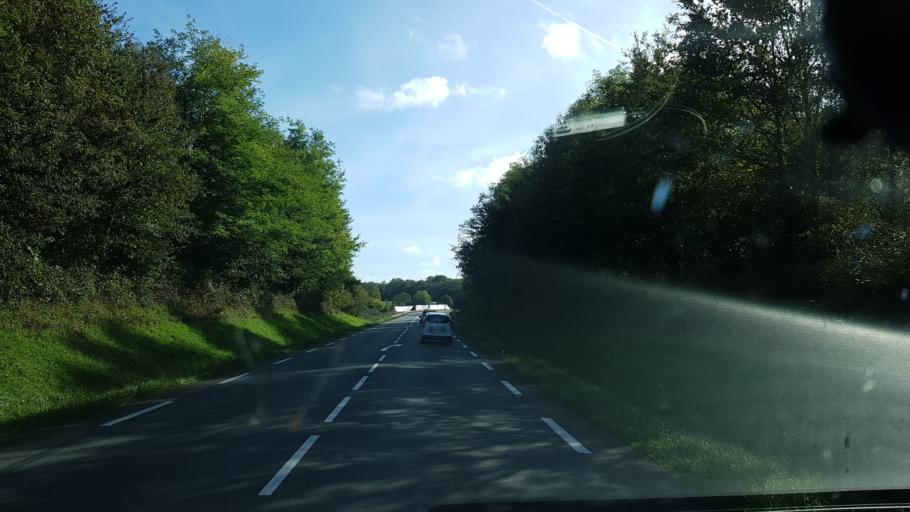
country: FR
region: Poitou-Charentes
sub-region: Departement de la Charente
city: Saint-Claud
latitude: 45.8644
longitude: 0.4663
